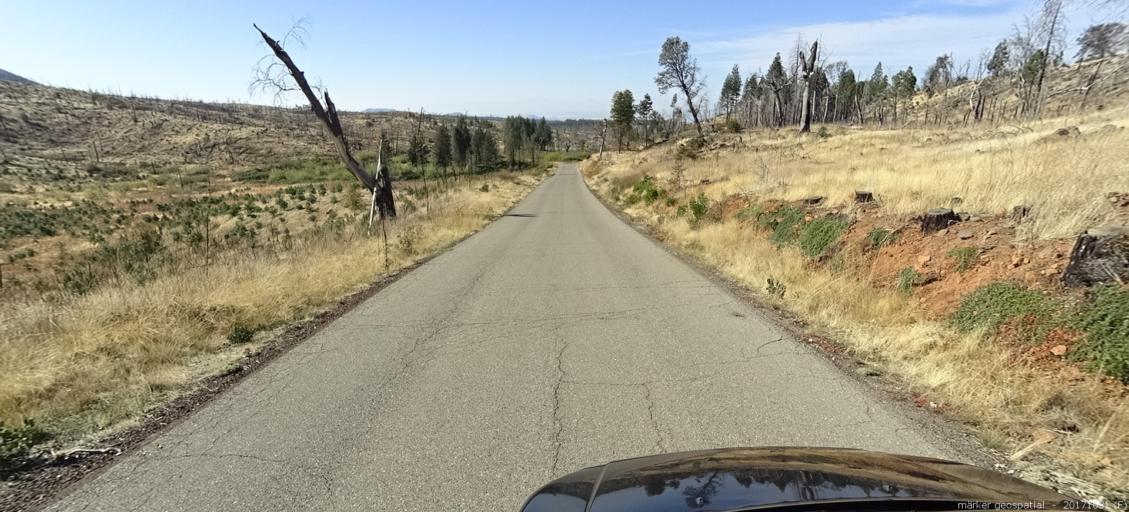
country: US
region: California
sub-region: Shasta County
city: Shingletown
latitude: 40.4569
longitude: -121.7849
